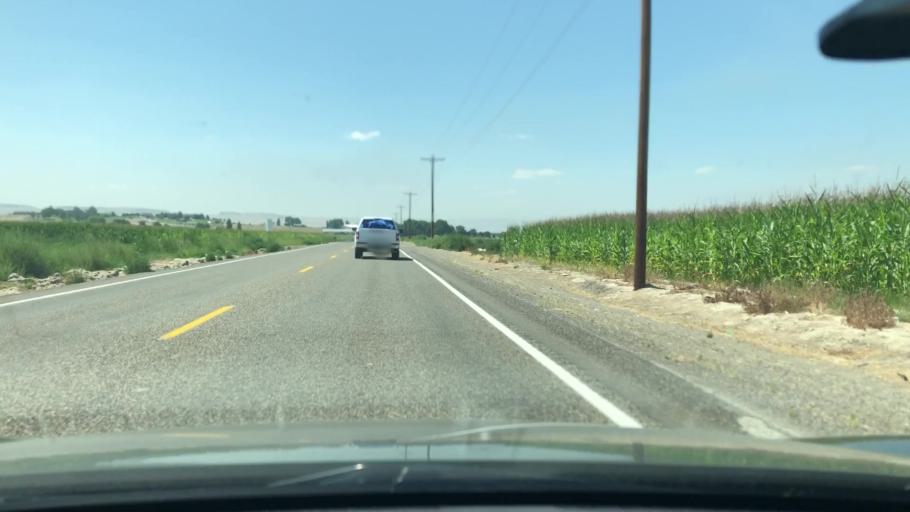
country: US
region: Idaho
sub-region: Owyhee County
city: Marsing
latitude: 43.5453
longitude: -116.8801
